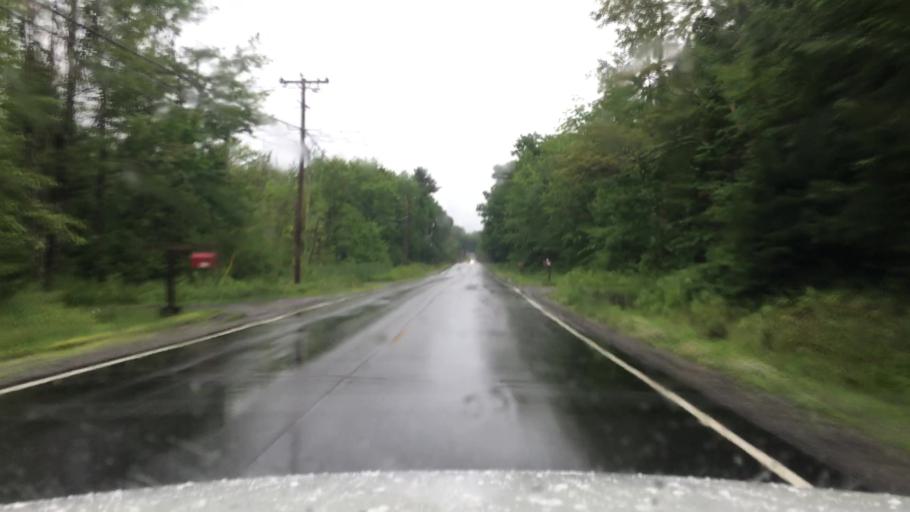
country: US
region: Maine
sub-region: Kennebec County
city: Manchester
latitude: 44.3163
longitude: -69.8432
